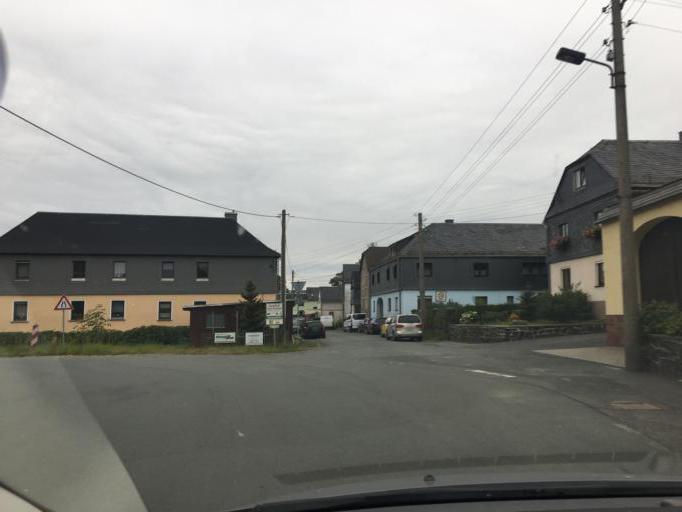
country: DE
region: Thuringia
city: Remptendorf
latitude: 50.4972
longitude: 11.6379
